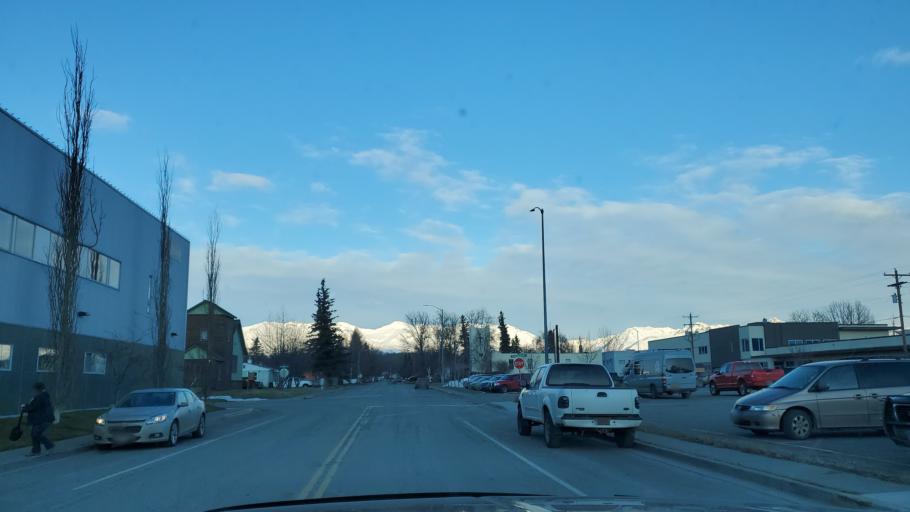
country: US
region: Alaska
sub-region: Matanuska-Susitna Borough
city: Palmer
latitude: 61.6010
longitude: -149.1165
